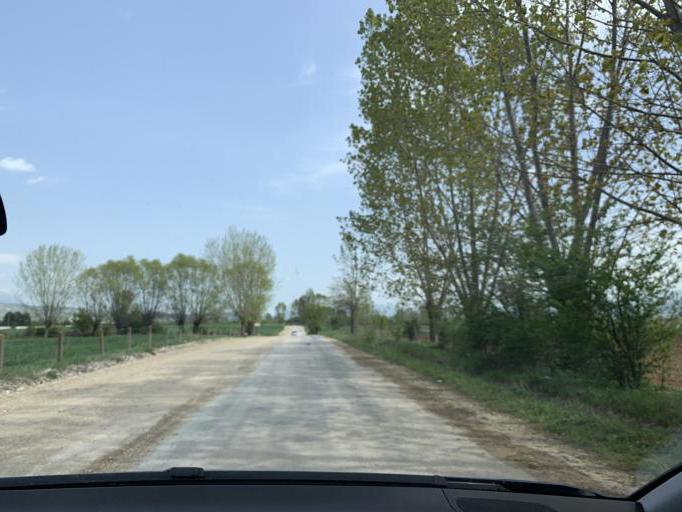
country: TR
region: Bolu
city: Bolu
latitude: 40.7479
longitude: 31.6645
